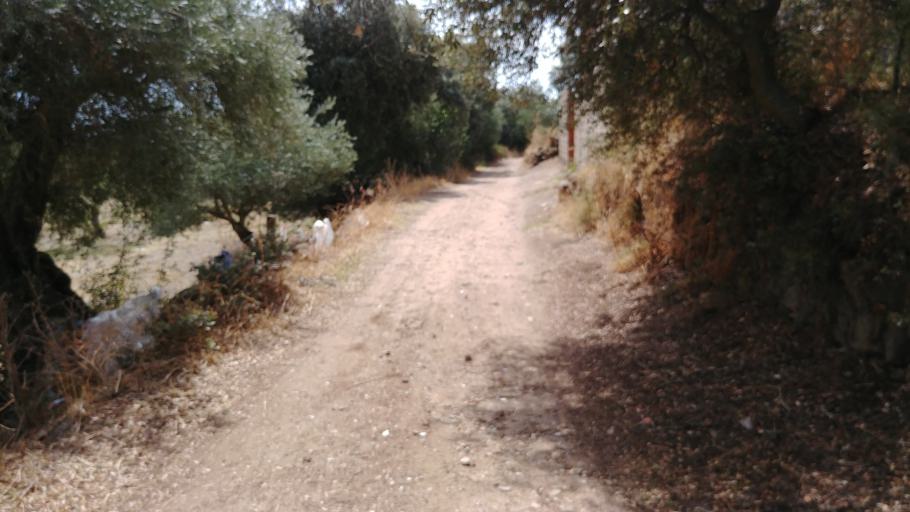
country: ES
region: Castille-La Mancha
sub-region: Province of Toledo
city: Navalcan
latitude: 40.0653
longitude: -5.0959
